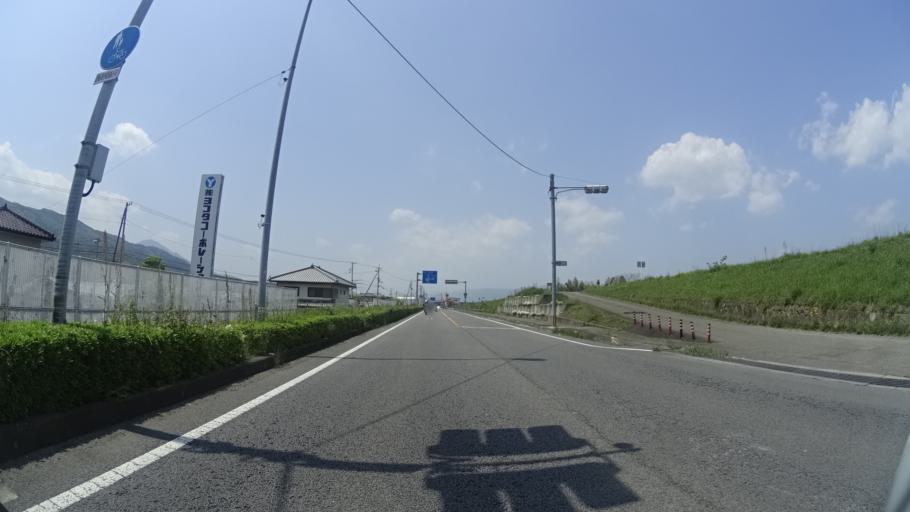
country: JP
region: Tokushima
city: Kamojimacho-jogejima
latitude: 34.0630
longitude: 134.2862
